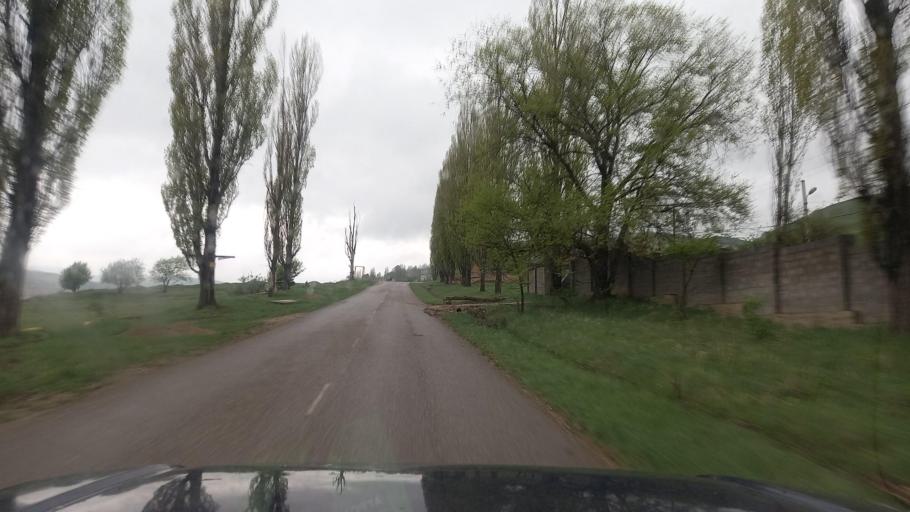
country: RU
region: Stavropol'skiy
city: Nezhinskiy
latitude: 43.8748
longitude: 42.6737
